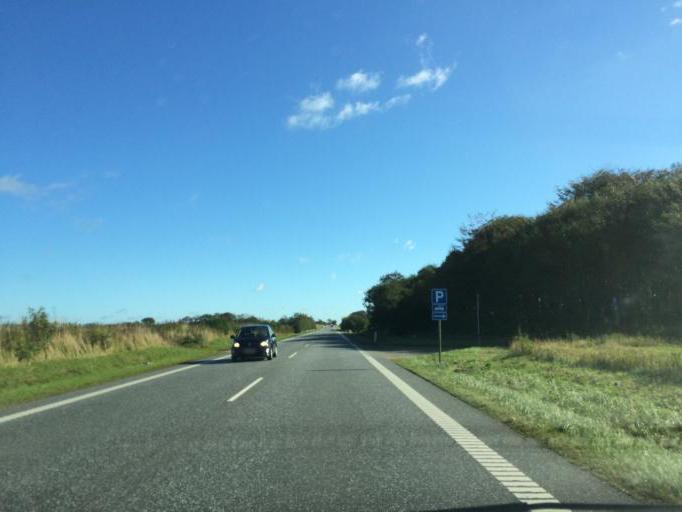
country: DK
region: Central Jutland
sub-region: Holstebro Kommune
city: Vinderup
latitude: 56.4004
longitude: 8.9222
